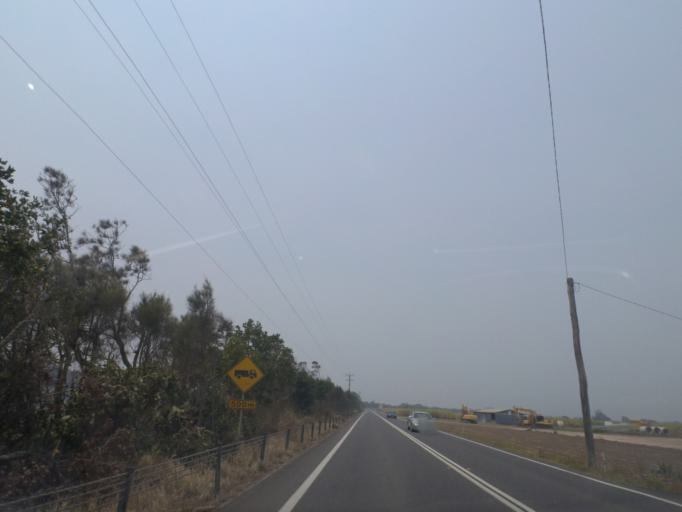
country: AU
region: New South Wales
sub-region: Richmond Valley
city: Evans Head
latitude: -28.9950
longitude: 153.4570
